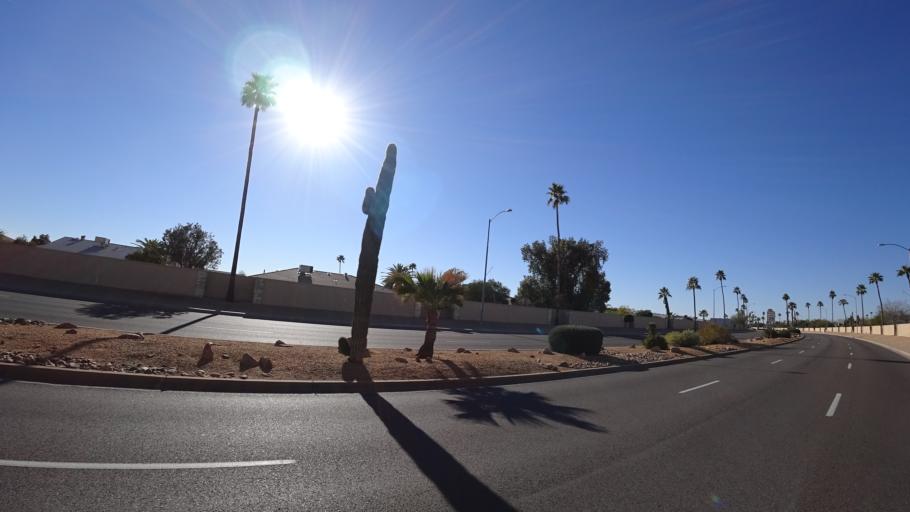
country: US
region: Arizona
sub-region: Maricopa County
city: Sun City West
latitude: 33.6504
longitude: -112.3383
